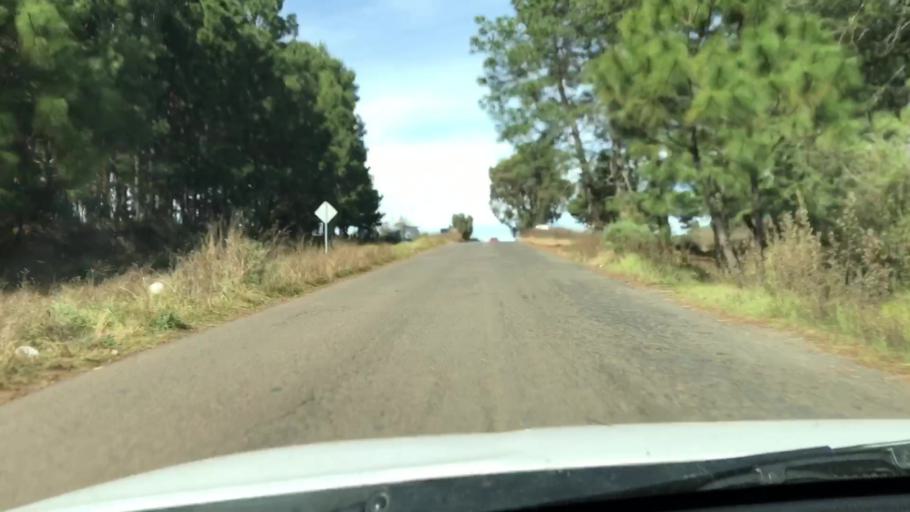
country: MX
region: Jalisco
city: Chiquilistlan
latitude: 20.1211
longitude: -103.7235
